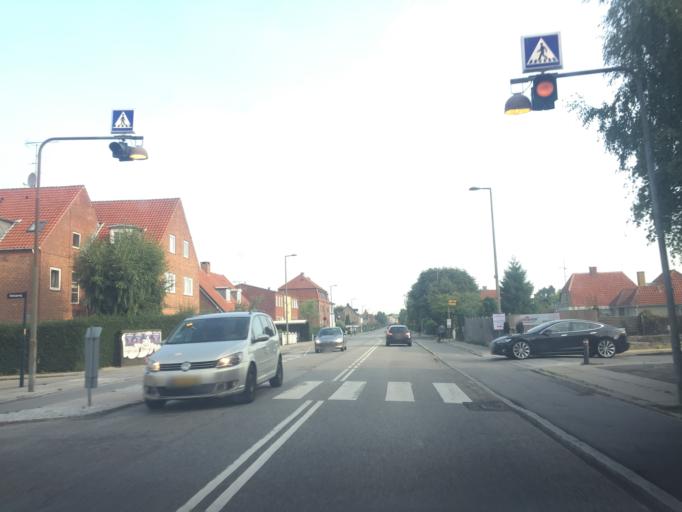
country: DK
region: Capital Region
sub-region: Kobenhavn
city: Vanlose
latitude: 55.7026
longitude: 12.4794
